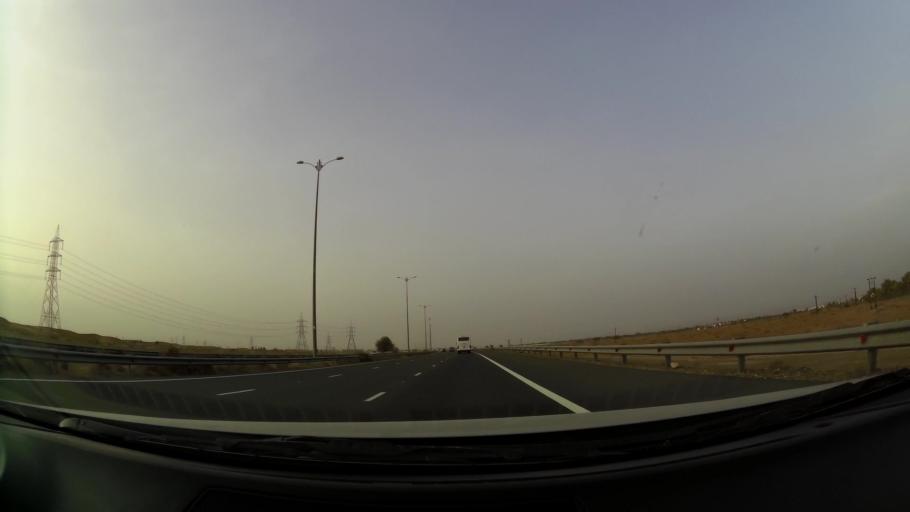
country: OM
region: Al Buraimi
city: Al Buraymi
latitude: 24.3680
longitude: 55.7932
